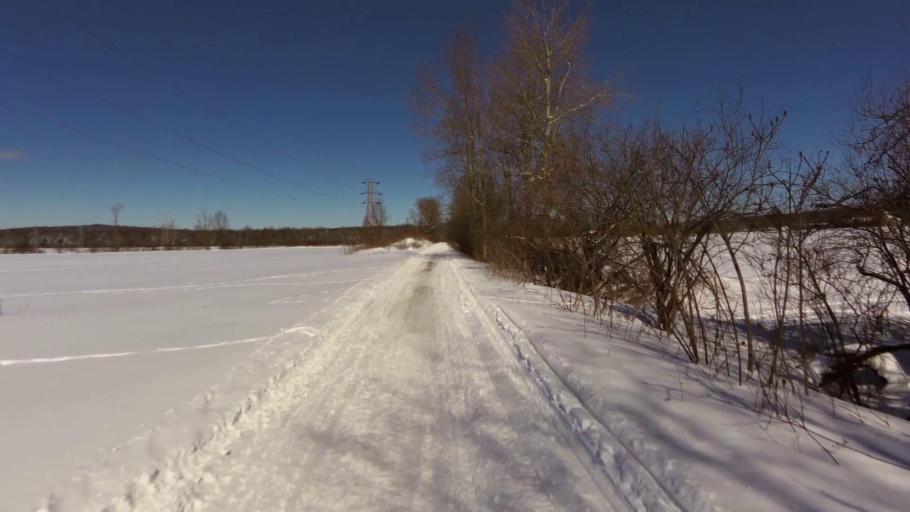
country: US
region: New York
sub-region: Chautauqua County
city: Celoron
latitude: 42.2338
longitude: -79.2690
